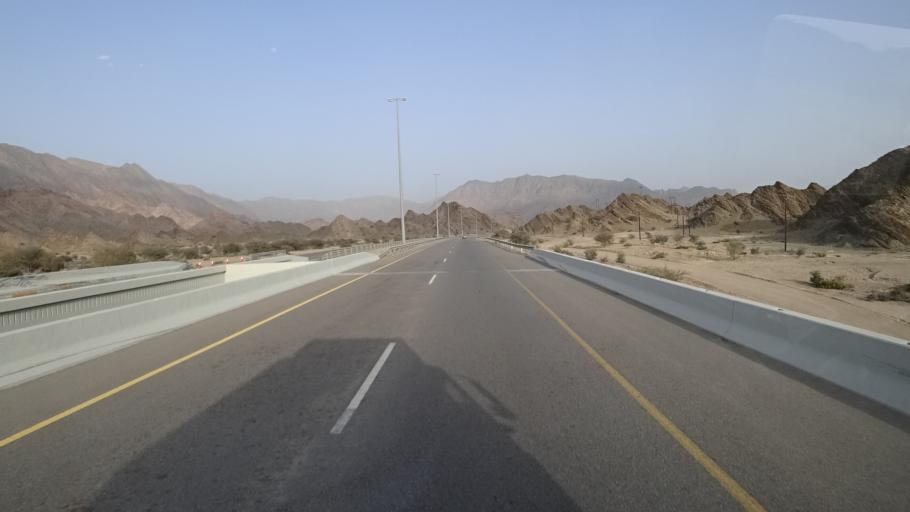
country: OM
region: Muhafazat Masqat
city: Muscat
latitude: 23.3319
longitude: 58.7096
